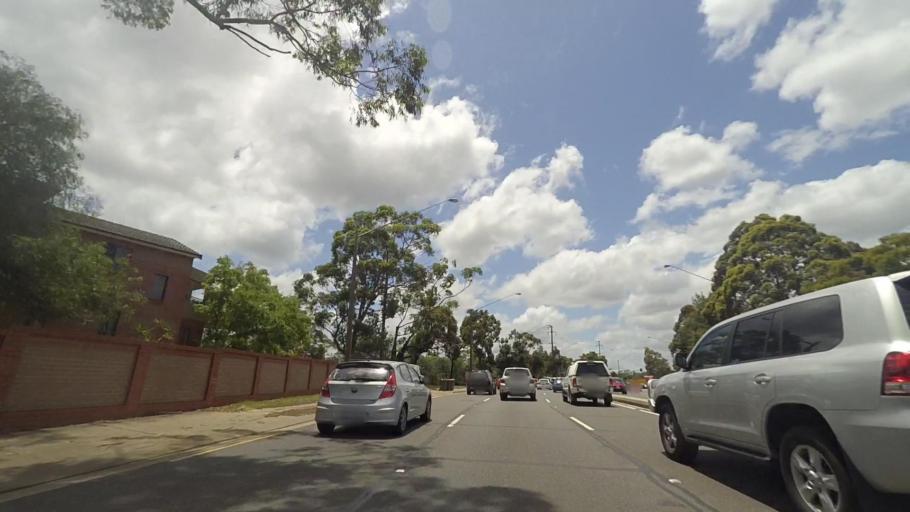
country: AU
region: New South Wales
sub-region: Hornsby Shire
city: Pennant Hills
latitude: -33.7342
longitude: 151.0769
